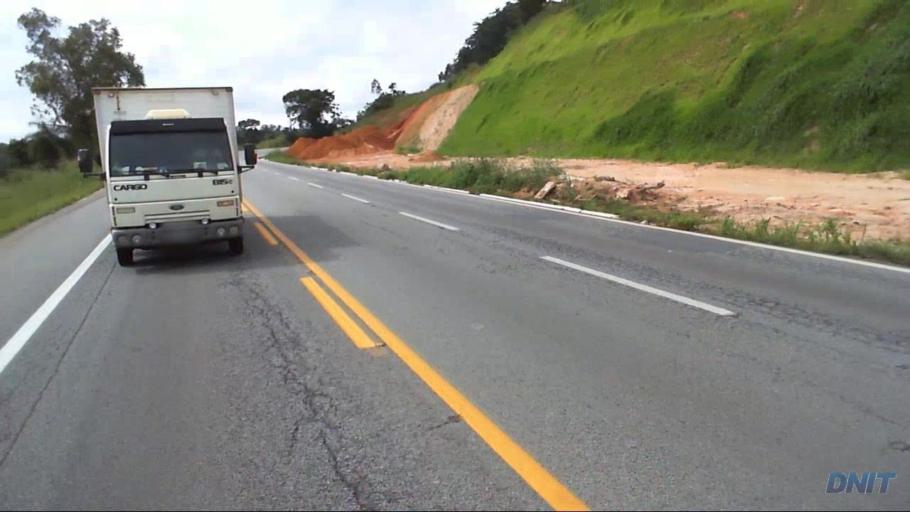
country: BR
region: Minas Gerais
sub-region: Caete
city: Caete
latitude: -19.7428
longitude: -43.6141
